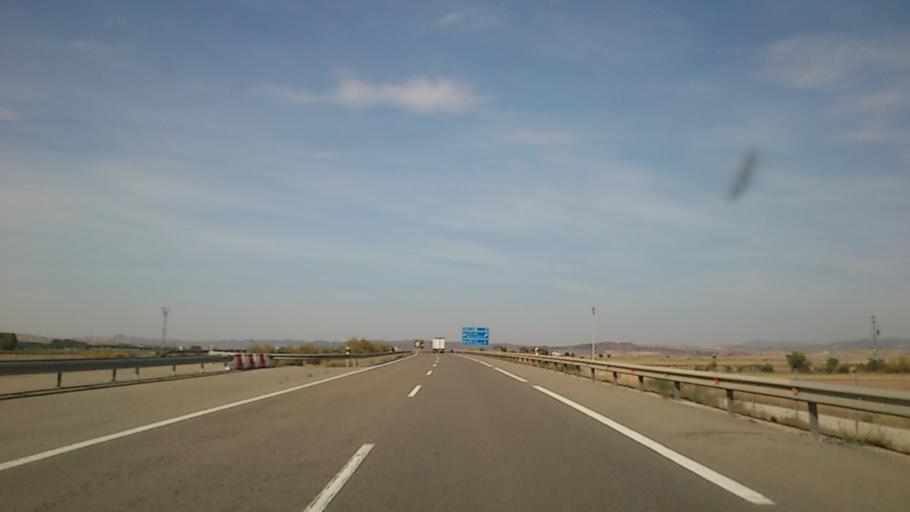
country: ES
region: Aragon
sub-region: Provincia de Teruel
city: Fuentes Claras
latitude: 40.8633
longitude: -1.3080
